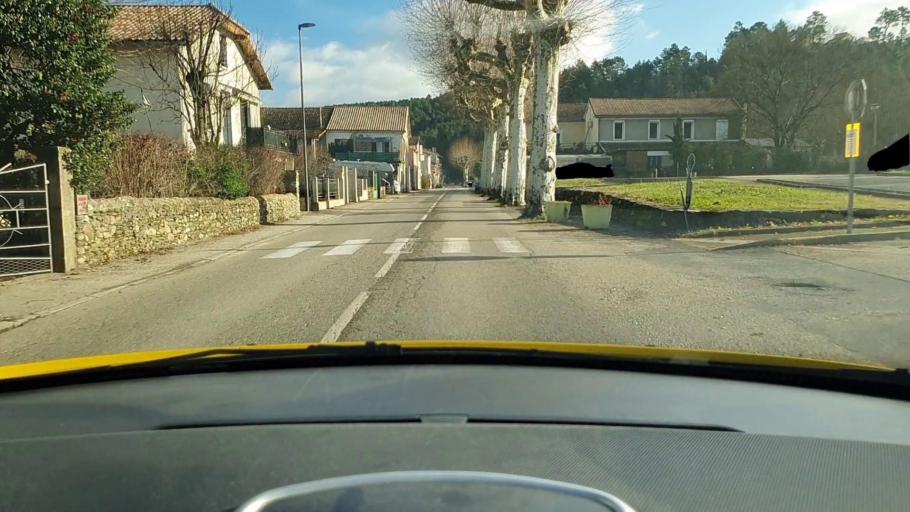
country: FR
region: Languedoc-Roussillon
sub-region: Departement du Gard
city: Branoux-les-Taillades
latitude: 44.3050
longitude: 3.9717
